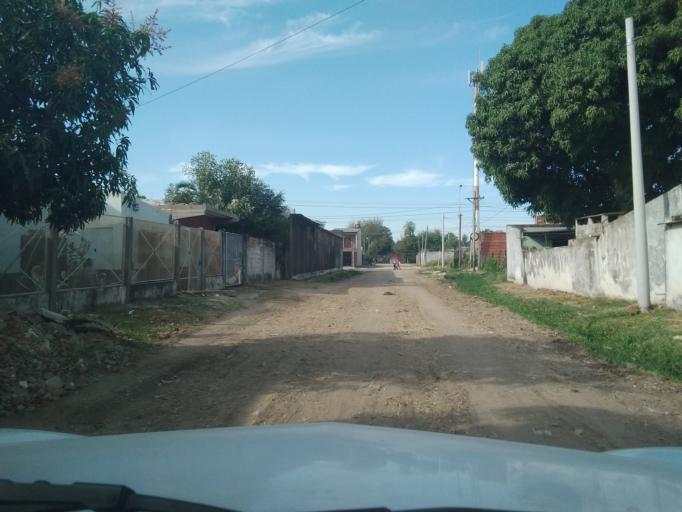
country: AR
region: Corrientes
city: Corrientes
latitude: -27.5054
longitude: -58.8069
